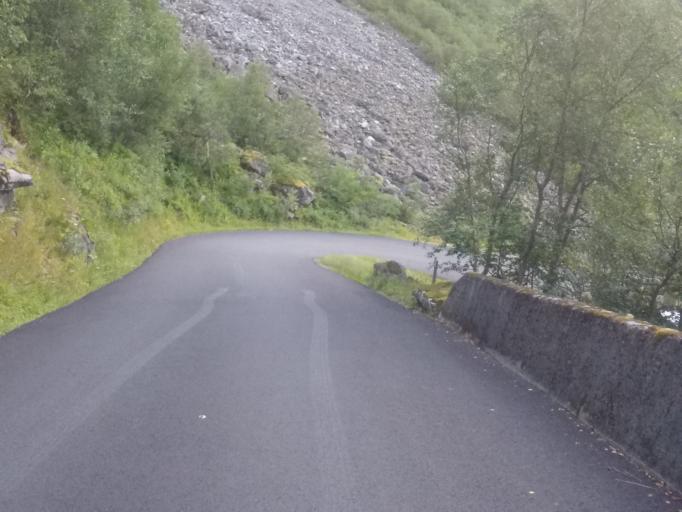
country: NO
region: More og Romsdal
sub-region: Norddal
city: Valldal
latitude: 61.9372
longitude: 7.2671
